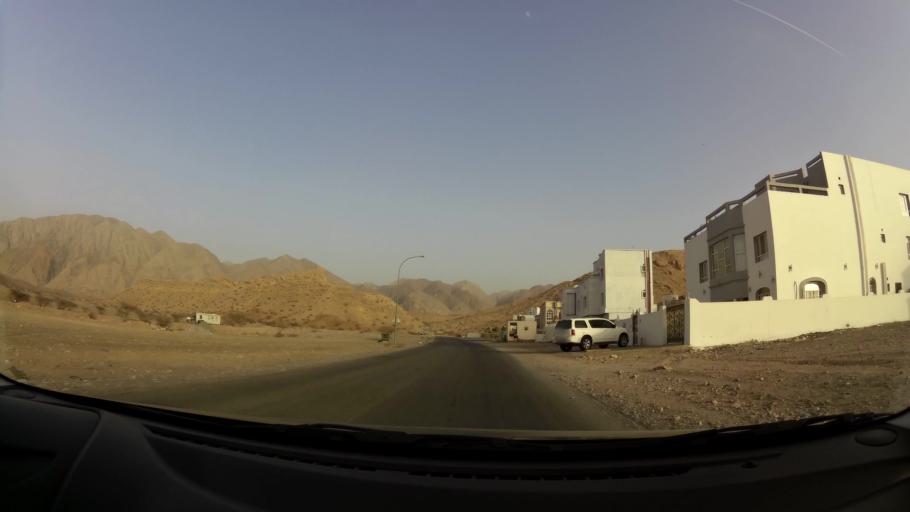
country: OM
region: Muhafazat Masqat
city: Bawshar
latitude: 23.5092
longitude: 58.3474
